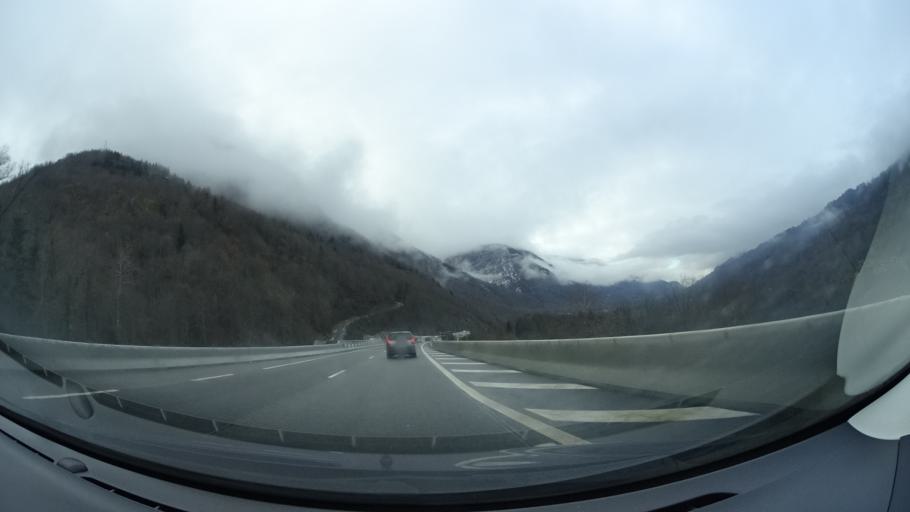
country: FR
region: Midi-Pyrenees
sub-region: Departement de l'Ariege
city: Ax-les-Thermes
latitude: 42.7245
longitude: 1.8221
